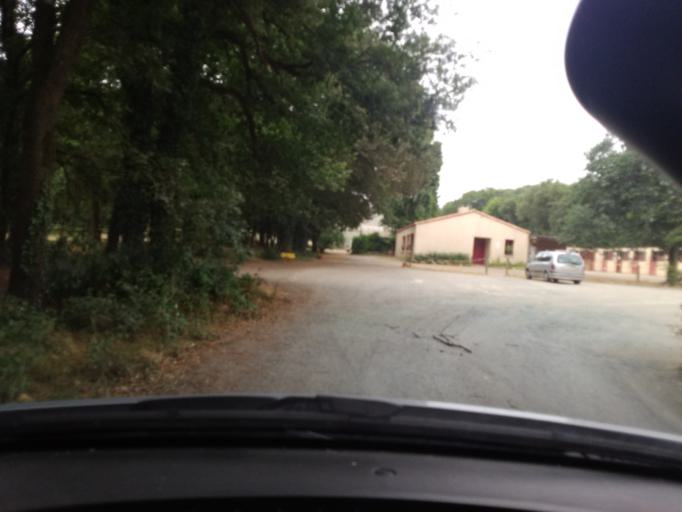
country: FR
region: Pays de la Loire
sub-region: Departement de la Vendee
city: Sainte-Gemme-la-Plaine
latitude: 46.4847
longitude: -1.1298
